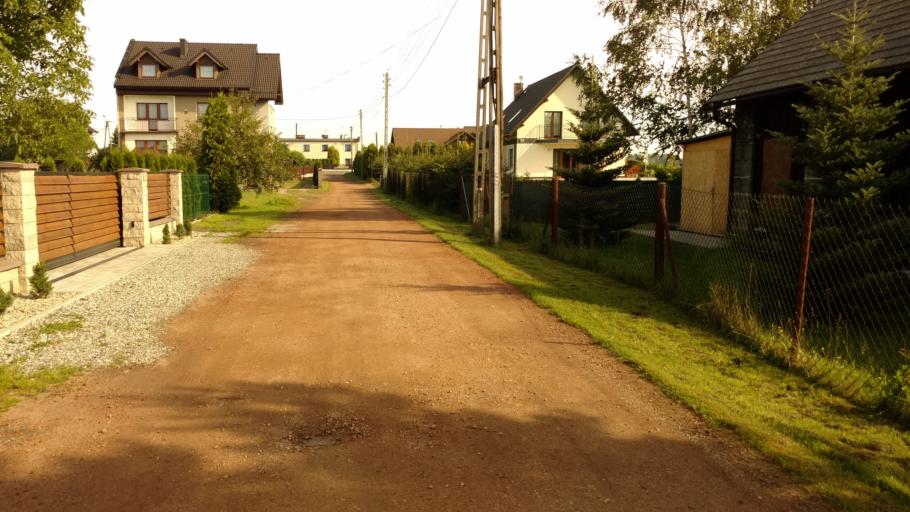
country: PL
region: Silesian Voivodeship
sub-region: Powiat pszczynski
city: Pszczyna
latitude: 49.9951
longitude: 18.9675
